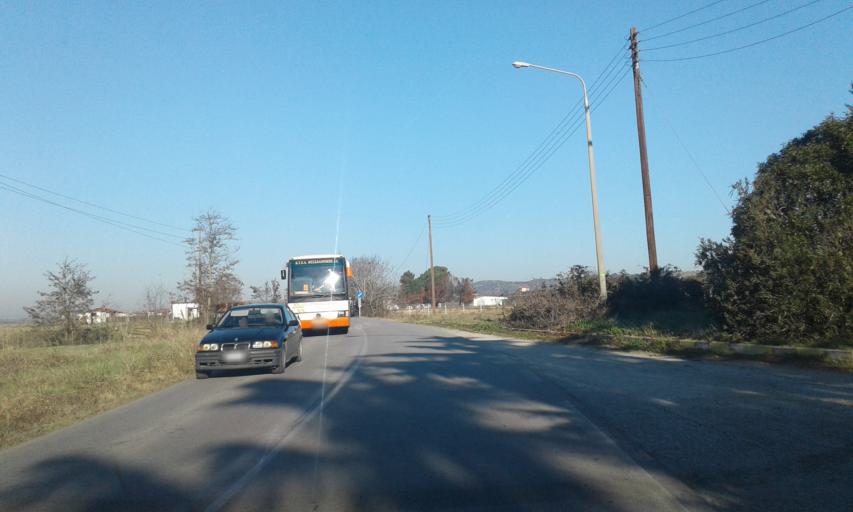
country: GR
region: Central Macedonia
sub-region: Nomos Thessalonikis
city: Kolchikon
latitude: 40.7432
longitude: 23.1414
